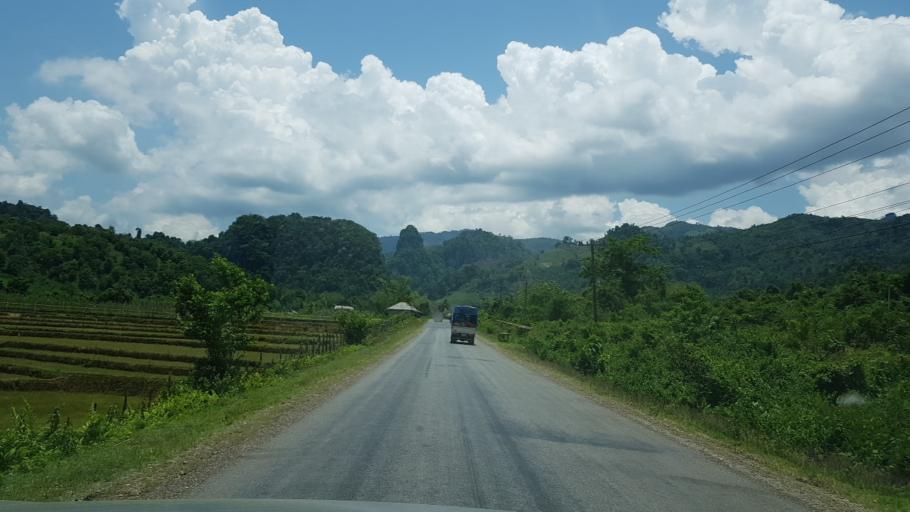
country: LA
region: Vientiane
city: Muang Kasi
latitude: 19.1262
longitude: 102.2468
